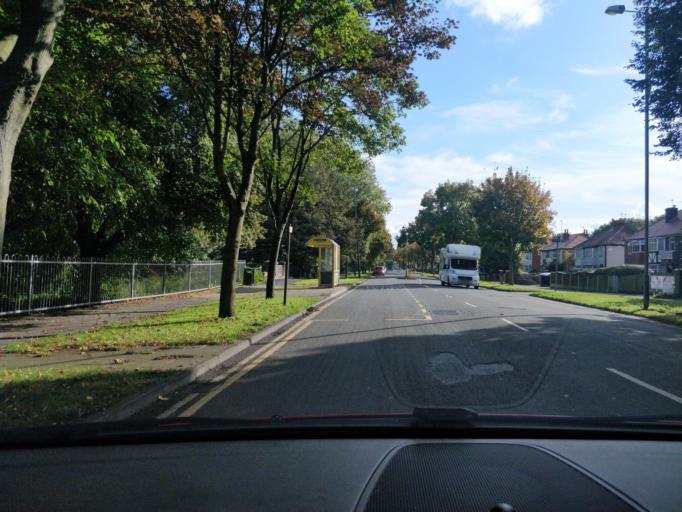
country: GB
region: England
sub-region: Sefton
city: Southport
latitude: 53.6354
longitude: -2.9774
